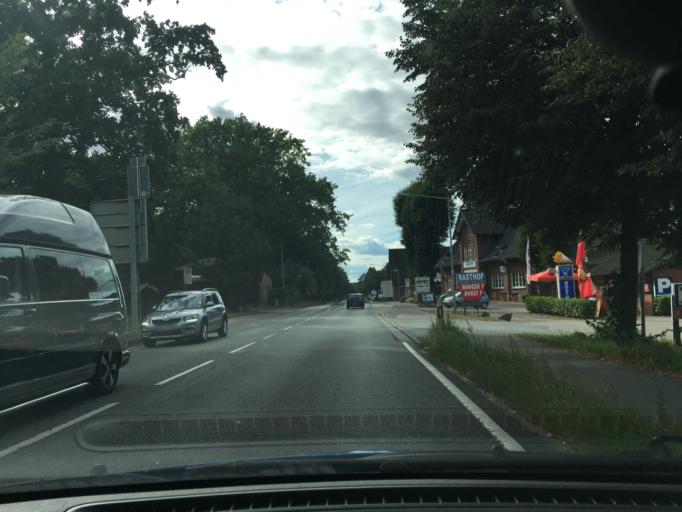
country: DE
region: Lower Saxony
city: Neu Wulmstorf
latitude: 53.4509
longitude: 9.7483
